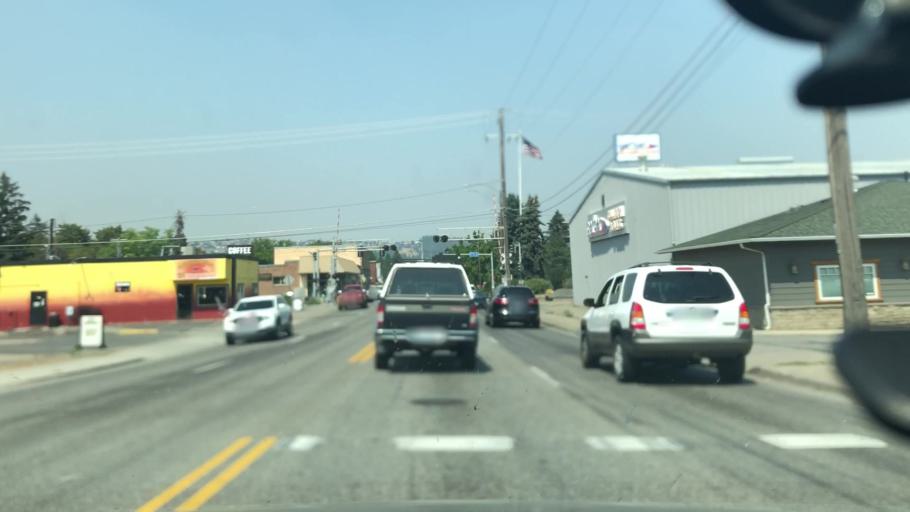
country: US
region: Washington
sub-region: Spokane County
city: Millwood
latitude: 47.6853
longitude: -117.2827
